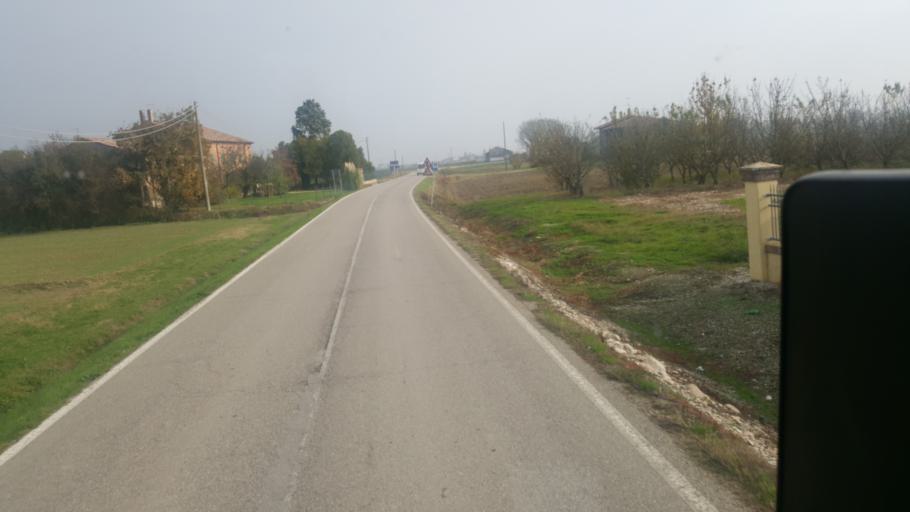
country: IT
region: Lombardy
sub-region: Provincia di Mantova
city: Sermide
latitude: 44.9584
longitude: 11.2560
